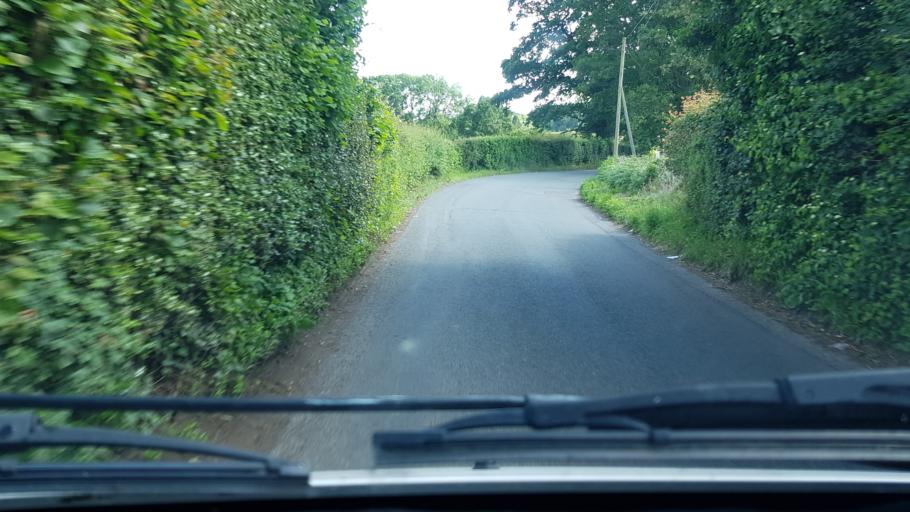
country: GB
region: England
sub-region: Worcestershire
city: Bewdley
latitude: 52.4111
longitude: -2.3070
